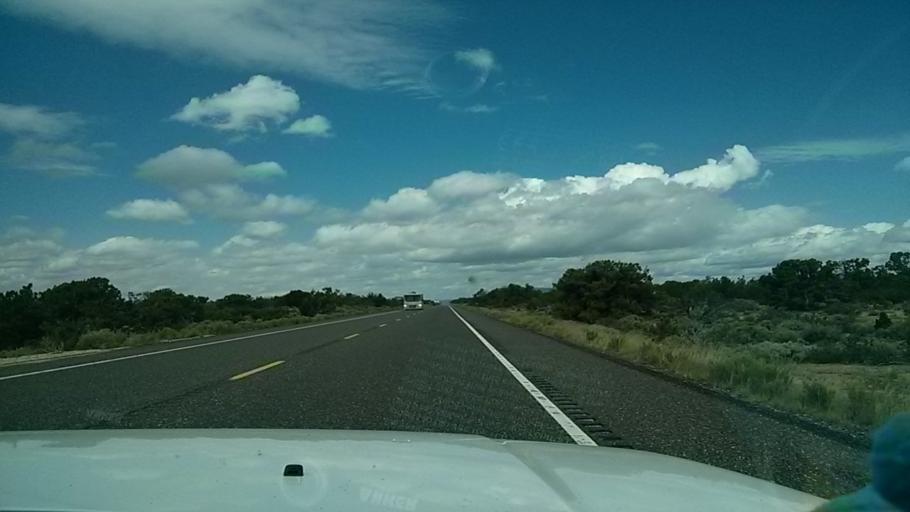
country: US
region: Utah
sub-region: Kane County
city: Kanab
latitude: 37.1741
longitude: -112.6212
